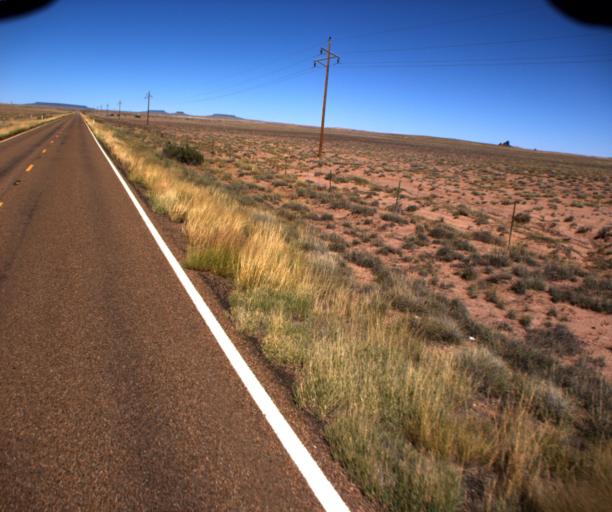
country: US
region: Arizona
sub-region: Navajo County
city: Holbrook
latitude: 35.0921
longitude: -110.0970
